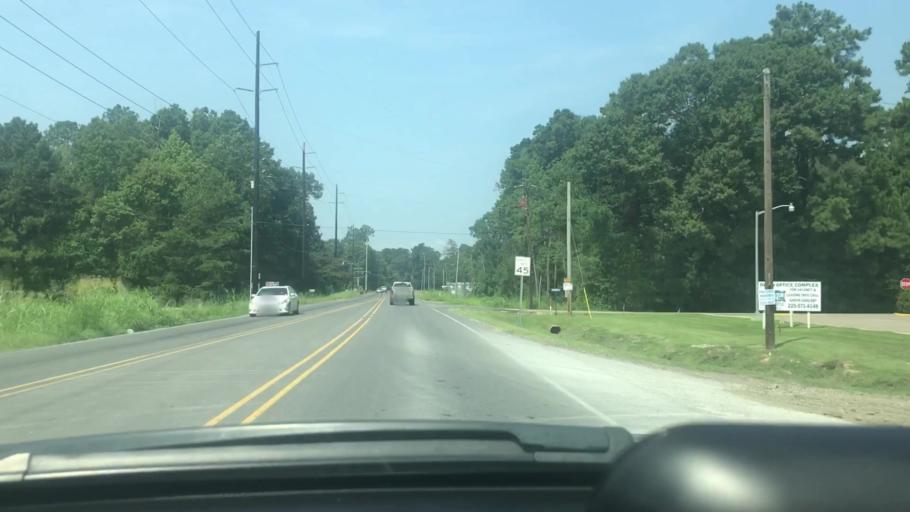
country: US
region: Louisiana
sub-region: Livingston Parish
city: Denham Springs
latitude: 30.4829
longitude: -90.9188
